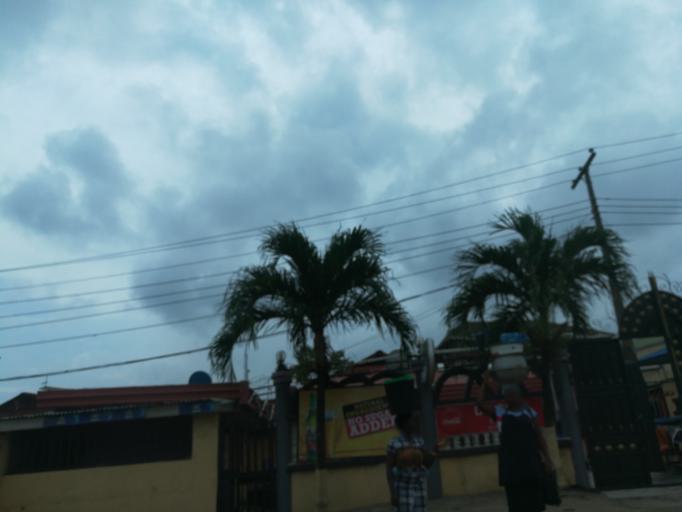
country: NG
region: Lagos
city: Oshodi
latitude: 6.5617
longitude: 3.3449
